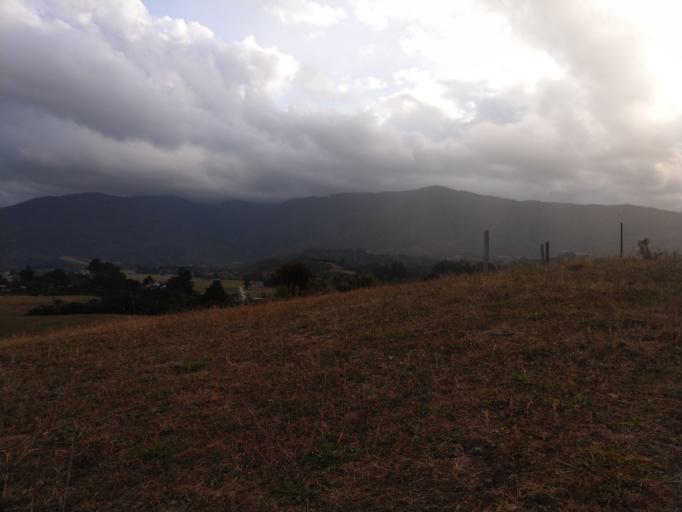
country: NZ
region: Tasman
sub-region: Tasman District
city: Takaka
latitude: -40.7893
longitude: 172.7447
